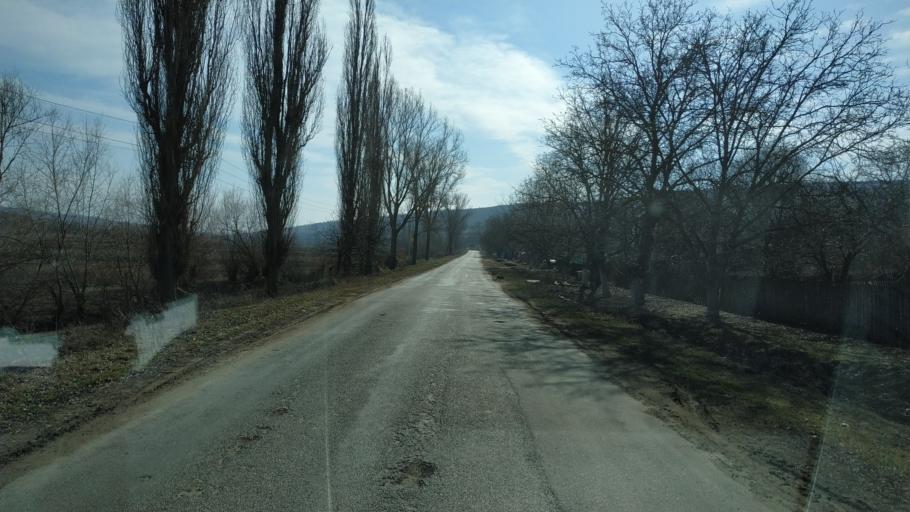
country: MD
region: Nisporeni
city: Nisporeni
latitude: 47.1532
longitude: 28.1079
